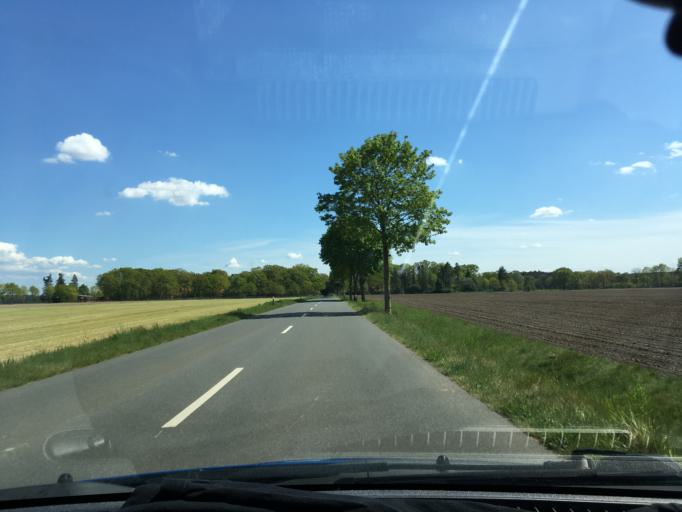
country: DE
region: Lower Saxony
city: Himbergen
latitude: 53.0889
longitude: 10.7361
